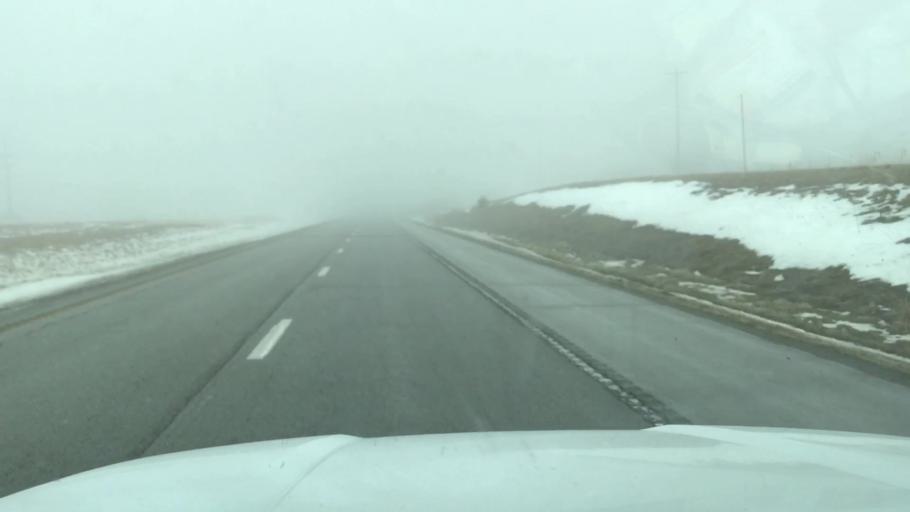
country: US
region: Missouri
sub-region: Clinton County
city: Cameron
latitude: 39.7550
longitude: -94.3082
